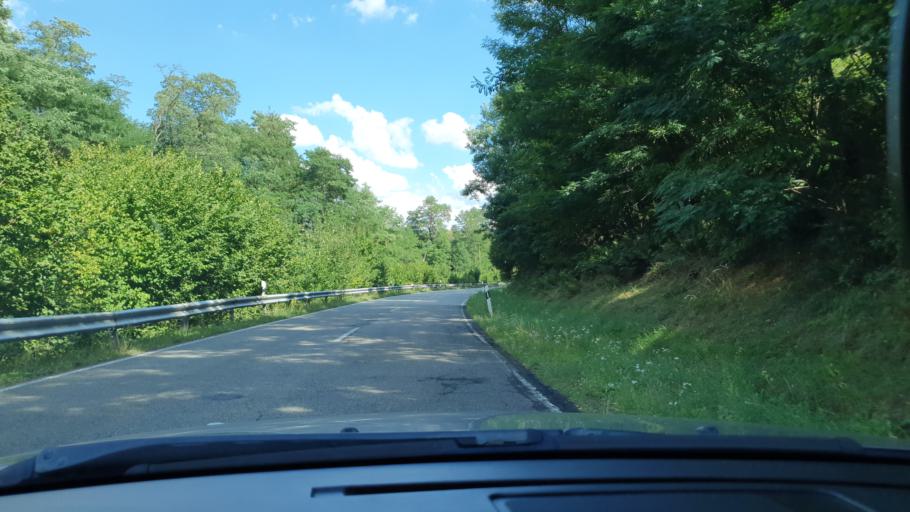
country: DE
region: Rheinland-Pfalz
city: Contwig
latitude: 49.2576
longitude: 7.4144
